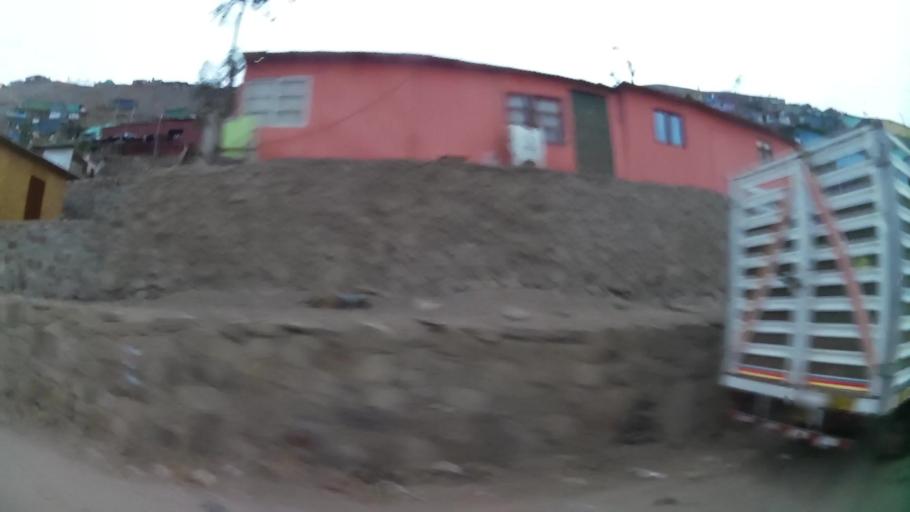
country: PE
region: Lima
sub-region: Lima
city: Surco
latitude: -12.1874
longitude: -77.0210
